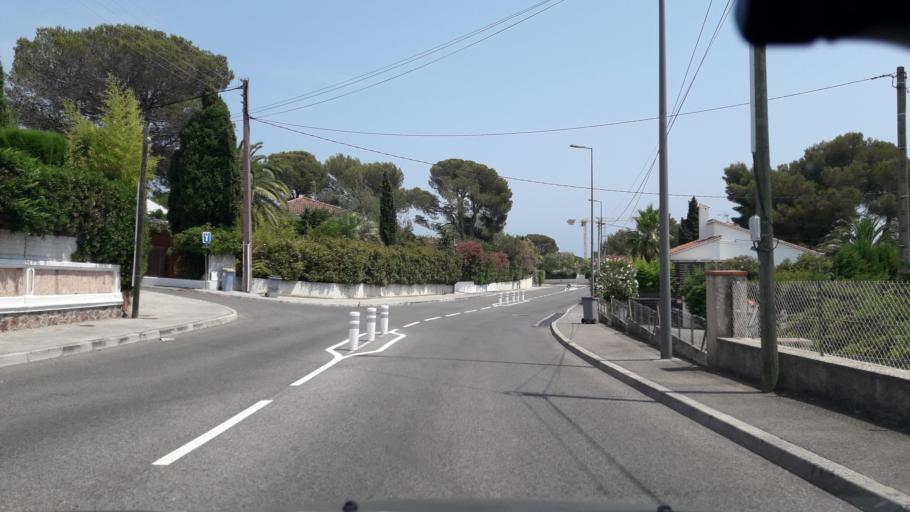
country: FR
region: Provence-Alpes-Cote d'Azur
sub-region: Departement du Var
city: Saint-Raphael
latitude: 43.4198
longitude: 6.7908
